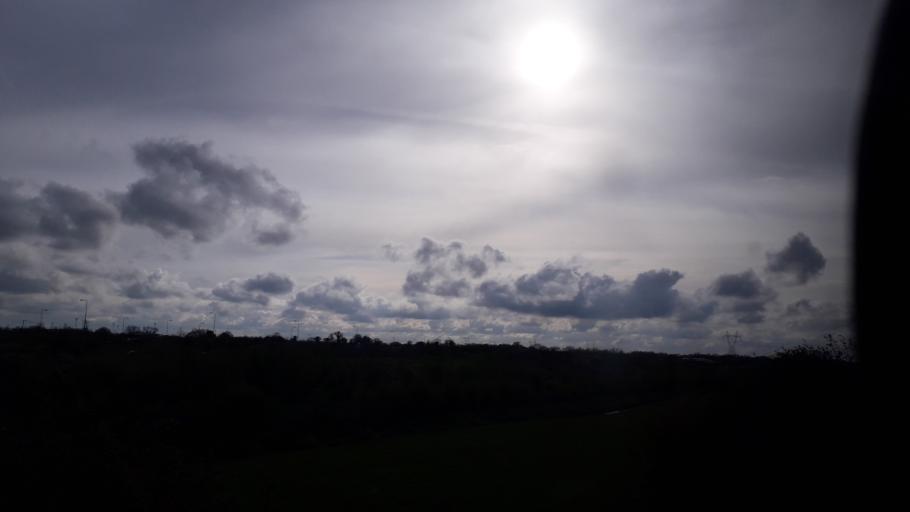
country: IE
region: Leinster
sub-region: An Mhi
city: Enfield
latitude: 53.4144
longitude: -6.8724
